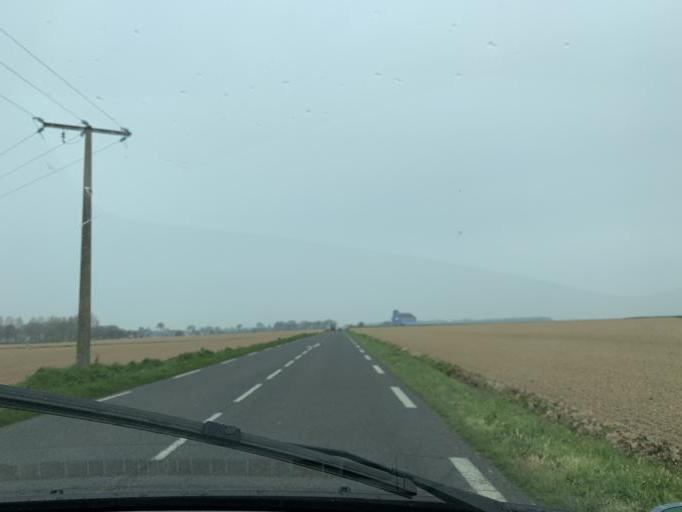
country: FR
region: Haute-Normandie
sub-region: Departement de la Seine-Maritime
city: Cany-Barville
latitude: 49.8120
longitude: 0.6693
